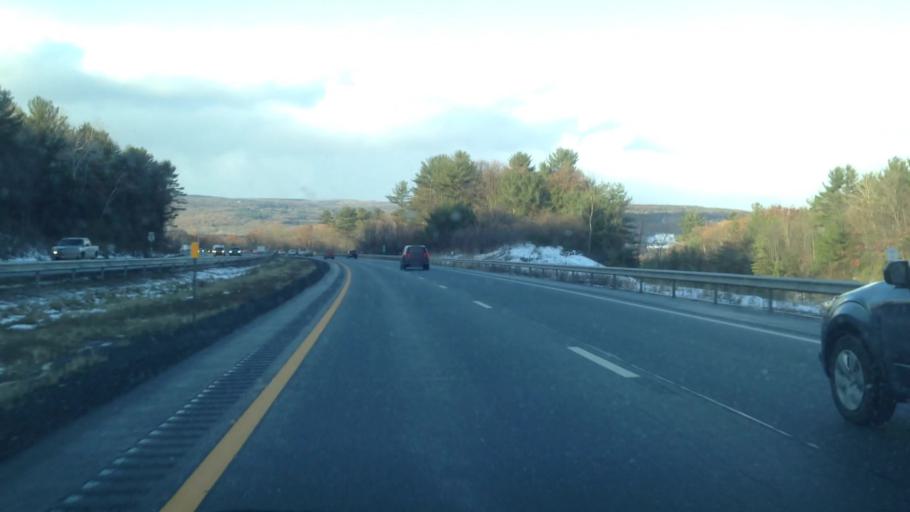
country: US
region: New York
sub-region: Schenectady County
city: Scotia
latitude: 42.8336
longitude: -74.0110
